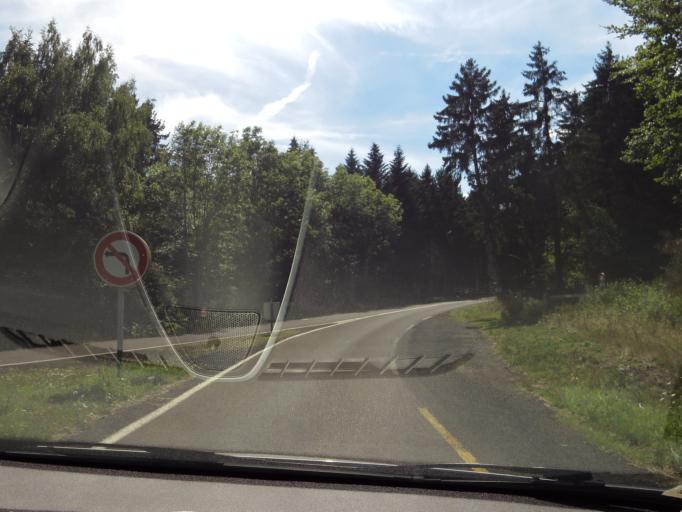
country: FR
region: Auvergne
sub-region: Departement du Puy-de-Dome
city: Orcines
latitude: 45.7682
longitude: 2.9861
